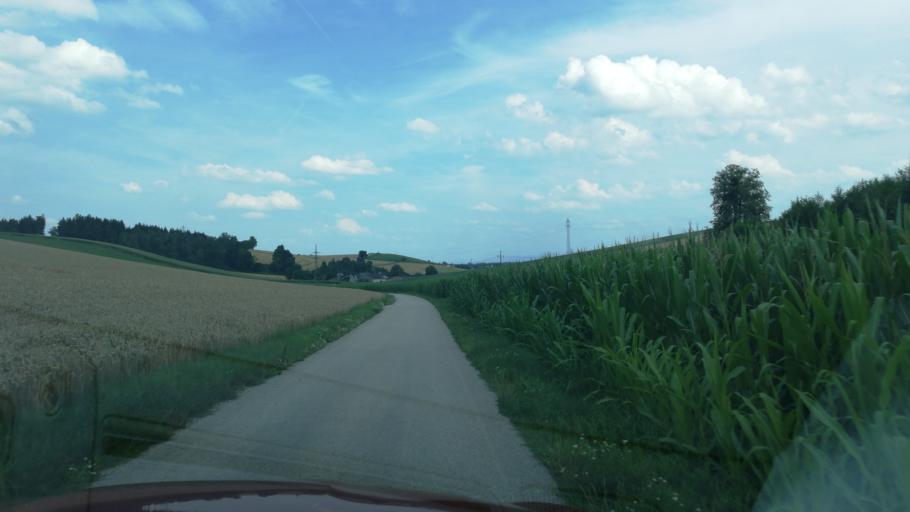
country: AT
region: Upper Austria
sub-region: Wels-Land
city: Neukirchen bei Lambach
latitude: 48.1105
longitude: 13.8342
